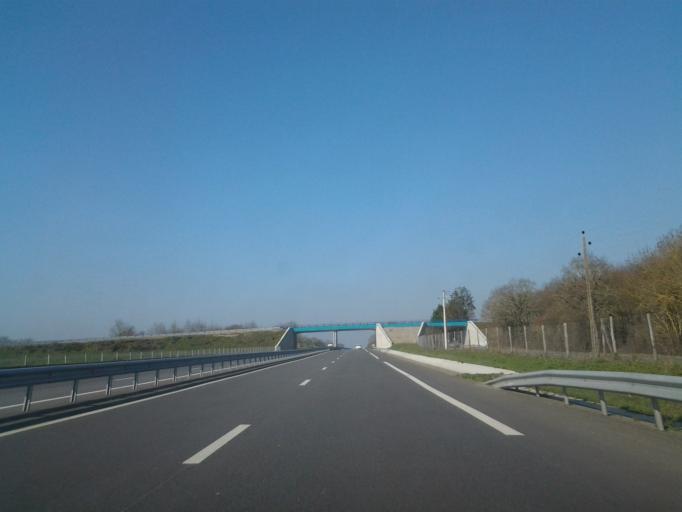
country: FR
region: Pays de la Loire
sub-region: Departement de la Vendee
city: Saint-Christophe-du-Ligneron
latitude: 46.8277
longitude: -1.7979
